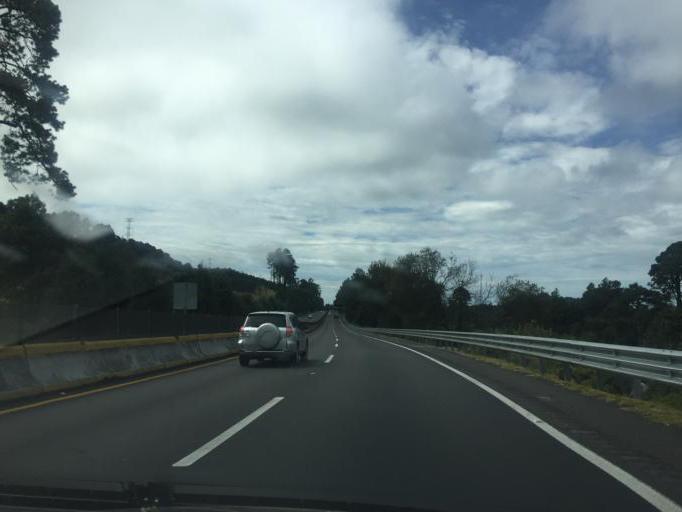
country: MX
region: Morelos
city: Tres Marias
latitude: 19.0820
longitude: -99.2318
